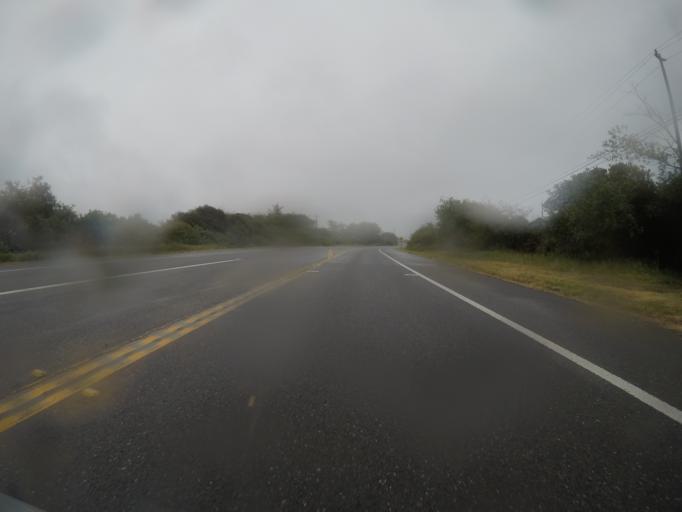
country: US
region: California
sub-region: Humboldt County
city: Eureka
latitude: 40.8634
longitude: -124.1545
